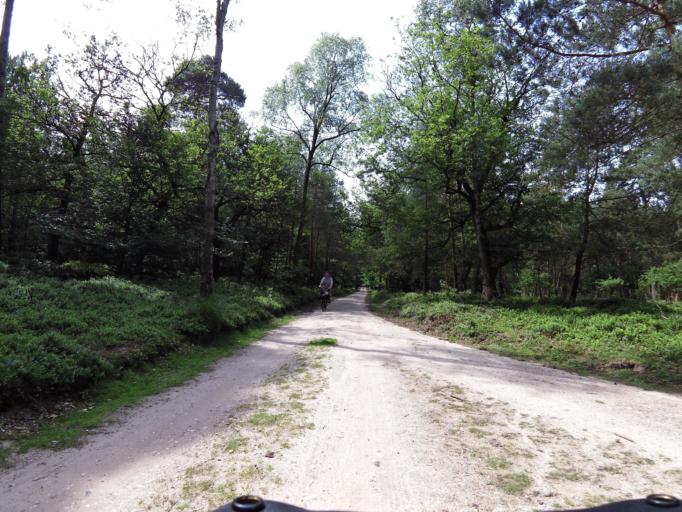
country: NL
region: Gelderland
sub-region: Gemeente Apeldoorn
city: Loenen
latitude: 52.0782
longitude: 5.9813
